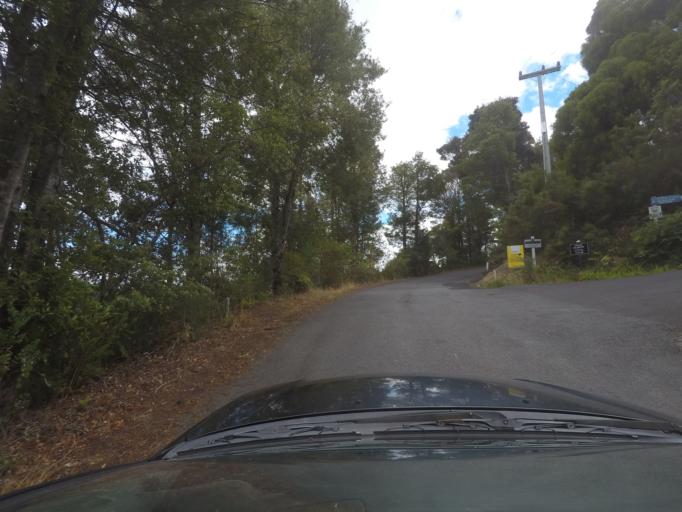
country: NZ
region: Northland
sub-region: Far North District
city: Paihia
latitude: -35.2893
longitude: 174.0970
